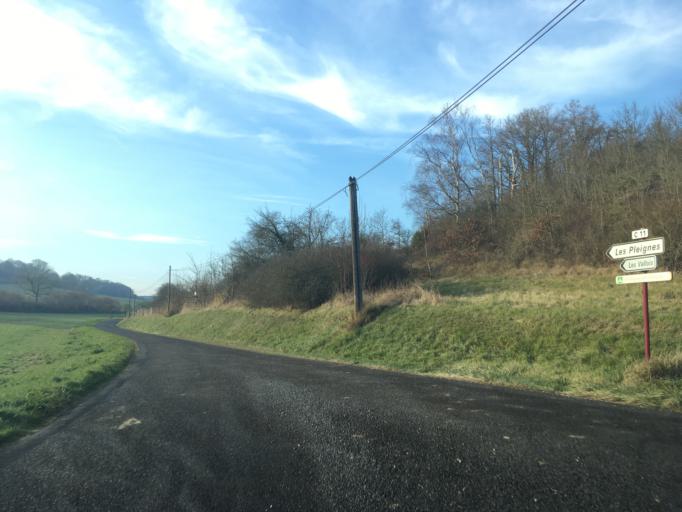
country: FR
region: Haute-Normandie
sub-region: Departement de l'Eure
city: Menilles
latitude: 49.0473
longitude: 1.2878
